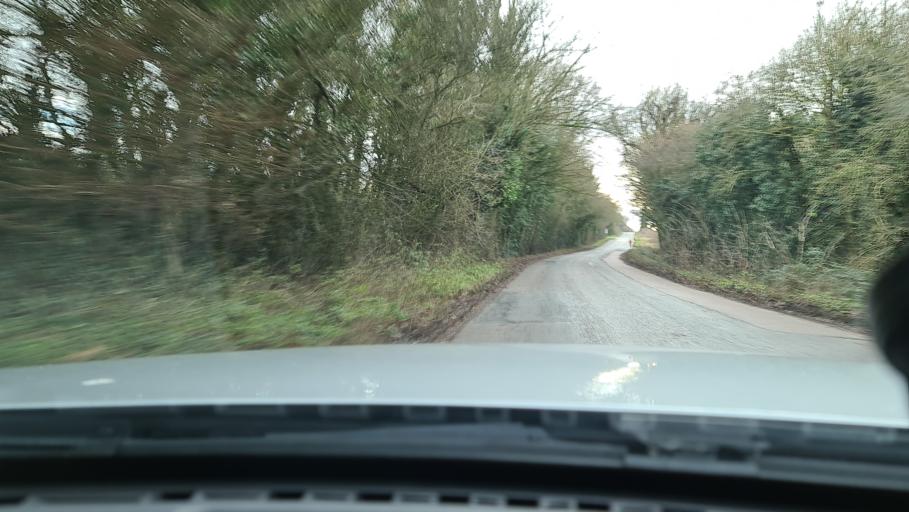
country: GB
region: England
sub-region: Oxfordshire
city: Banbury
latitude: 52.0867
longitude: -1.2753
